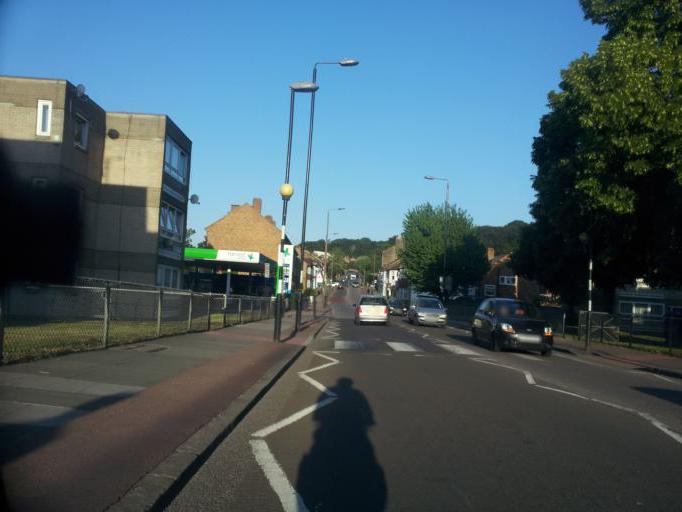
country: GB
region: England
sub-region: Greater London
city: Abbey Wood
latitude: 51.4853
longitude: 0.1039
